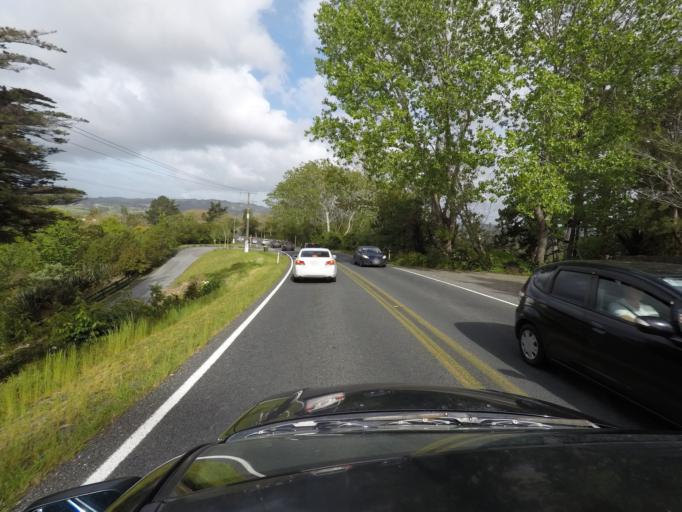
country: NZ
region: Auckland
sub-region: Auckland
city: Pakuranga
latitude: -36.9446
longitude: 174.9523
